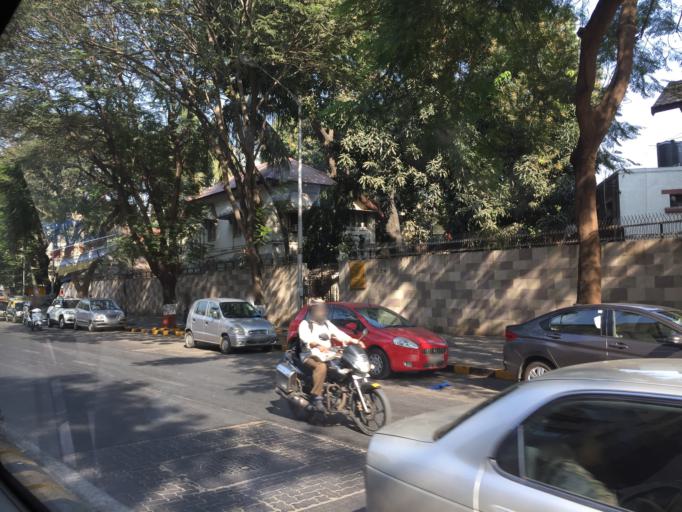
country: IN
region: Maharashtra
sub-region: Raigarh
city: Uran
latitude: 18.9338
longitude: 72.8370
